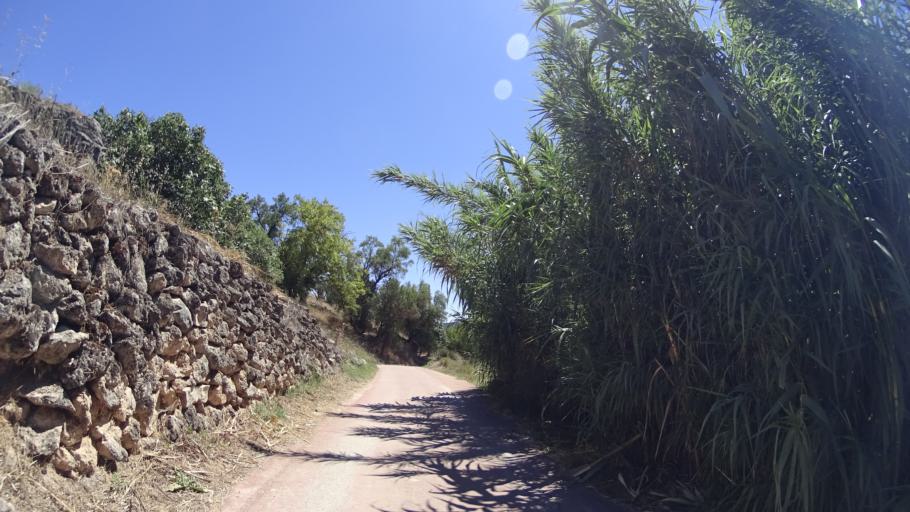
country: ES
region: Madrid
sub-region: Provincia de Madrid
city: Carabana
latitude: 40.2864
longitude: -3.2000
